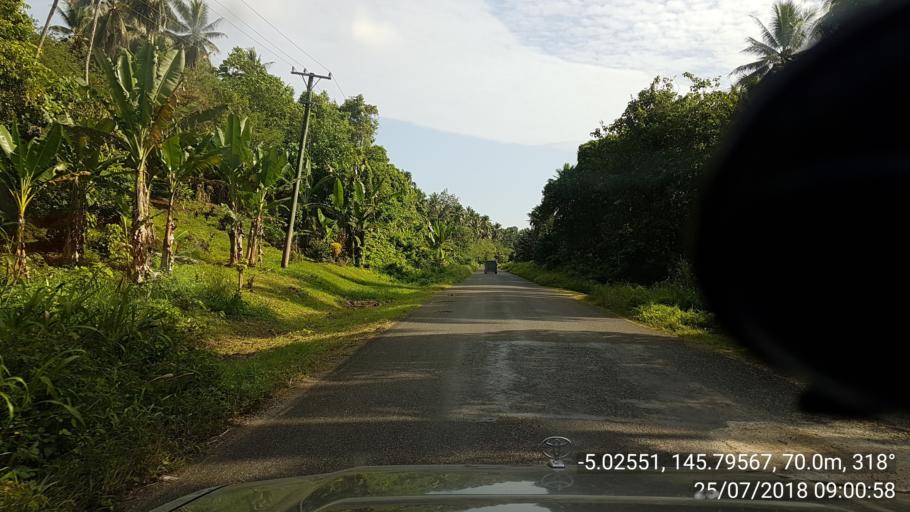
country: PG
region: Madang
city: Madang
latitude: -5.0256
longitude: 145.7958
